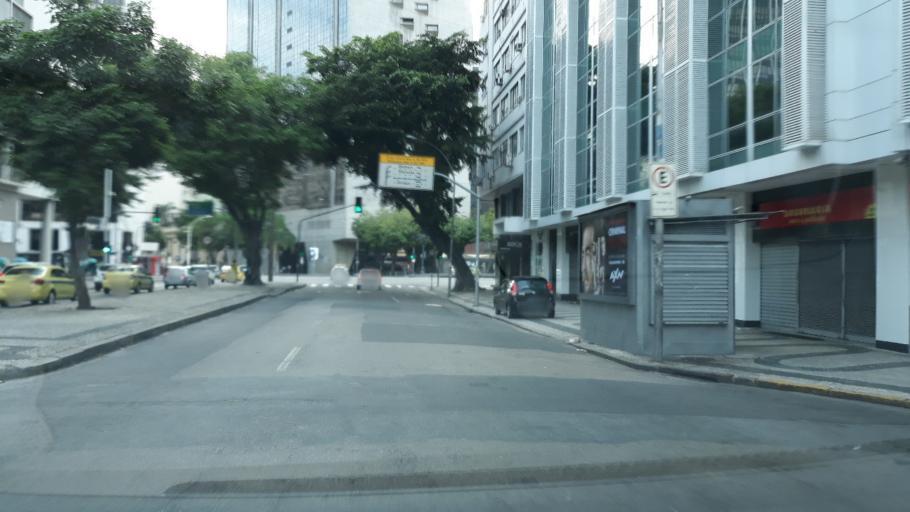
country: BR
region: Rio de Janeiro
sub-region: Rio De Janeiro
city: Rio de Janeiro
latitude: -22.9097
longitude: -43.1711
